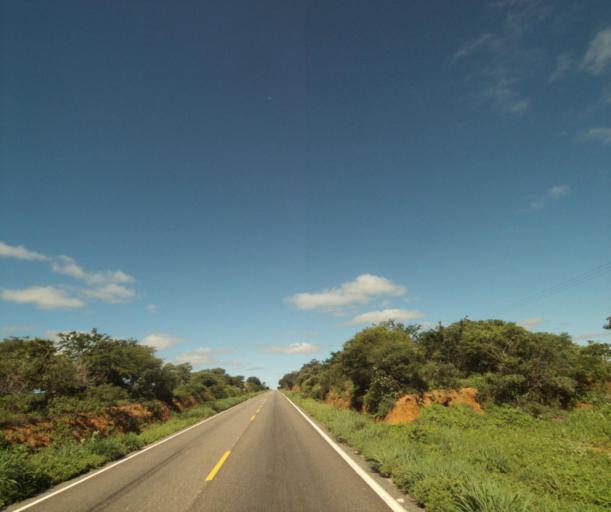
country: BR
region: Bahia
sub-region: Palmas De Monte Alto
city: Palmas de Monte Alto
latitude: -14.2364
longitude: -42.9989
